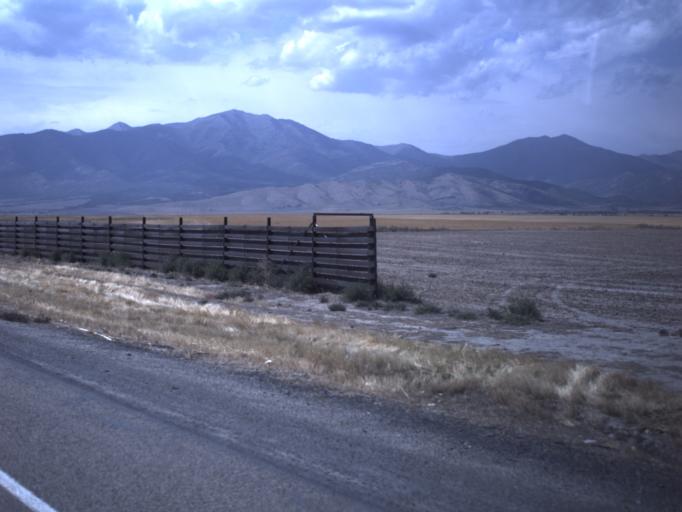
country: US
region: Utah
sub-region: Utah County
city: Eagle Mountain
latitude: 40.3698
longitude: -112.0275
